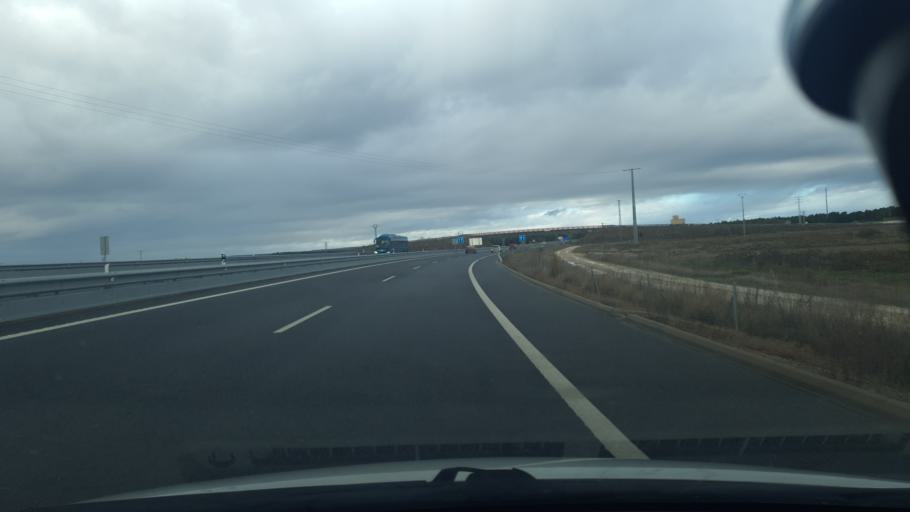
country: ES
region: Castille and Leon
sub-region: Provincia de Segovia
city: Sanchonuno
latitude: 41.3195
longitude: -4.3122
